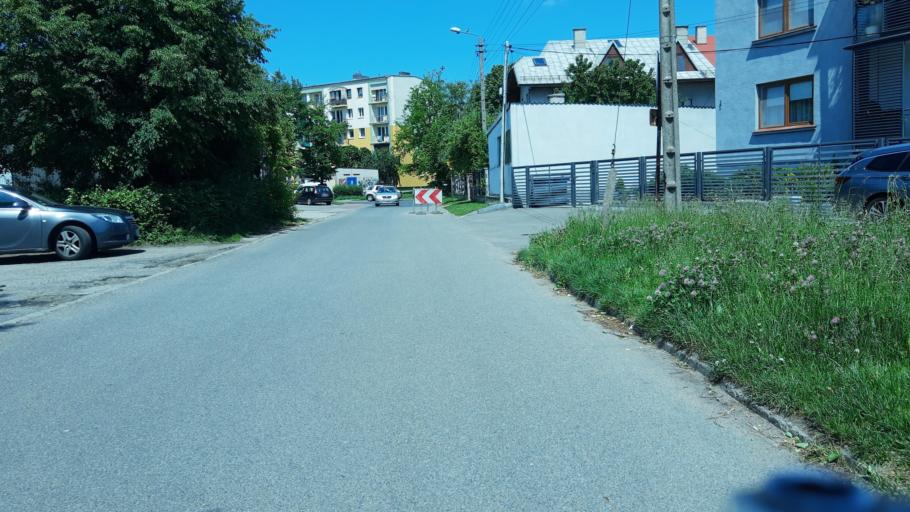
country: PL
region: Lodz Voivodeship
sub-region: Powiat sieradzki
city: Sieradz
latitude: 51.5858
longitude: 18.7273
